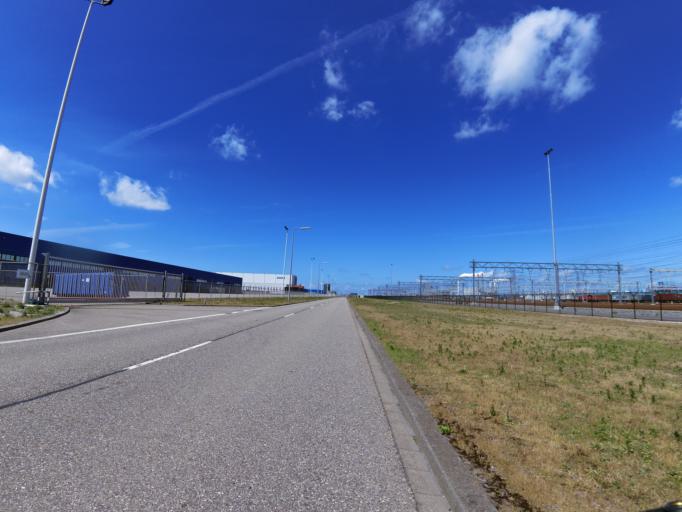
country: NL
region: South Holland
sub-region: Gemeente Rotterdam
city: Hoek van Holland
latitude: 51.9370
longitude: 4.0260
